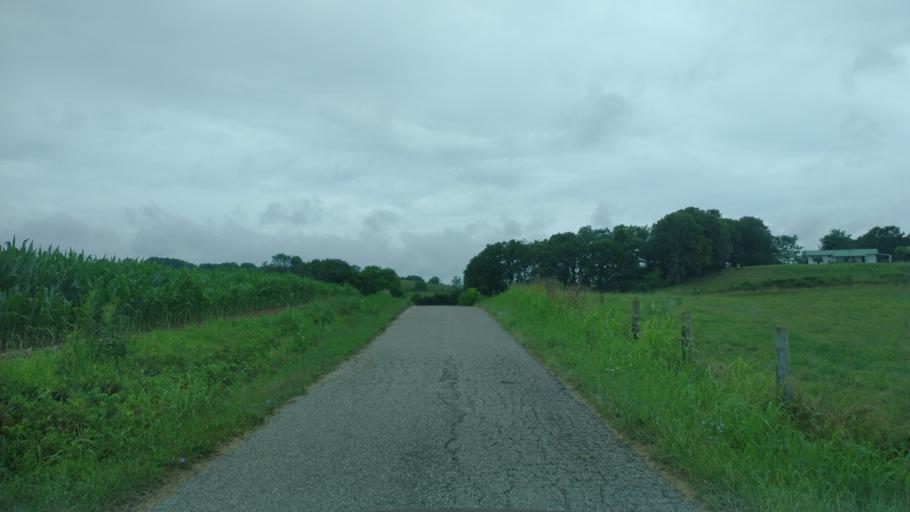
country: US
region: West Virginia
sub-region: Mason County
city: New Haven
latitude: 38.9243
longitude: -81.9530
